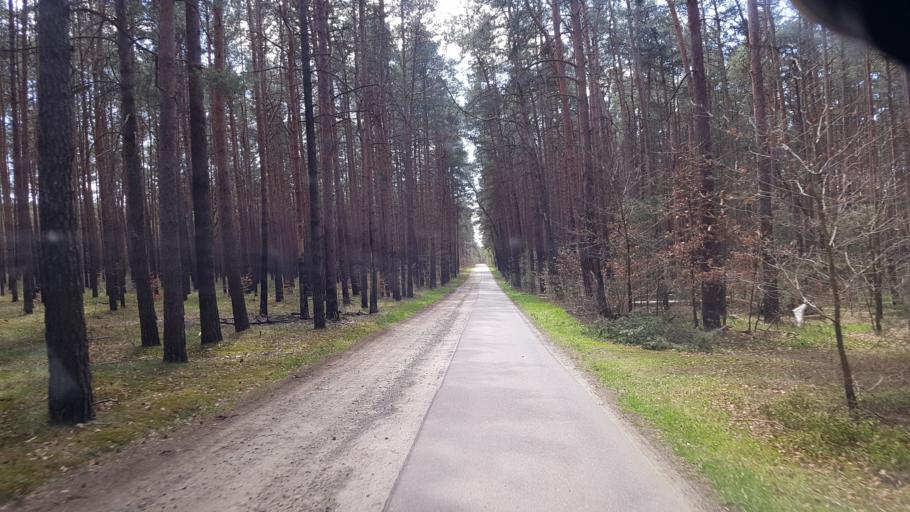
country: DE
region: Brandenburg
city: Schonborn
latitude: 51.5362
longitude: 13.4733
